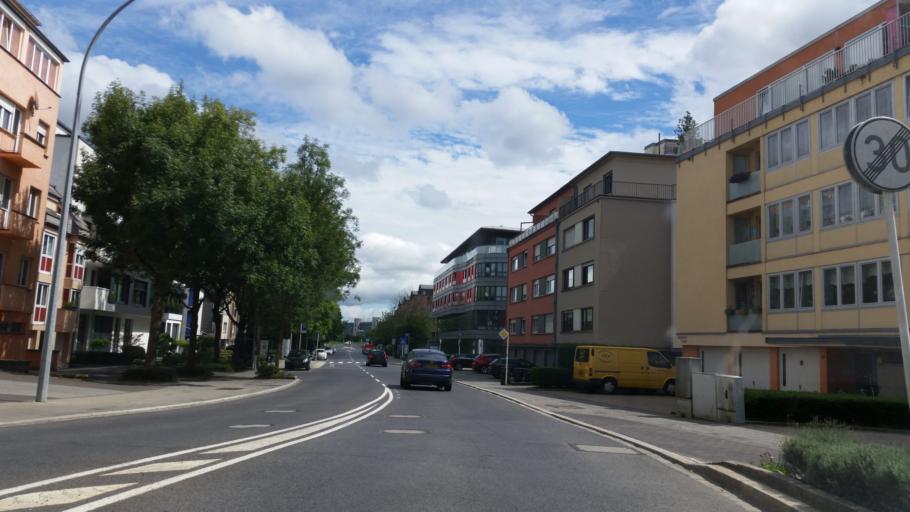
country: LU
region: Luxembourg
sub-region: Canton de Luxembourg
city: Luxembourg
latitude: 49.6022
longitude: 6.1001
